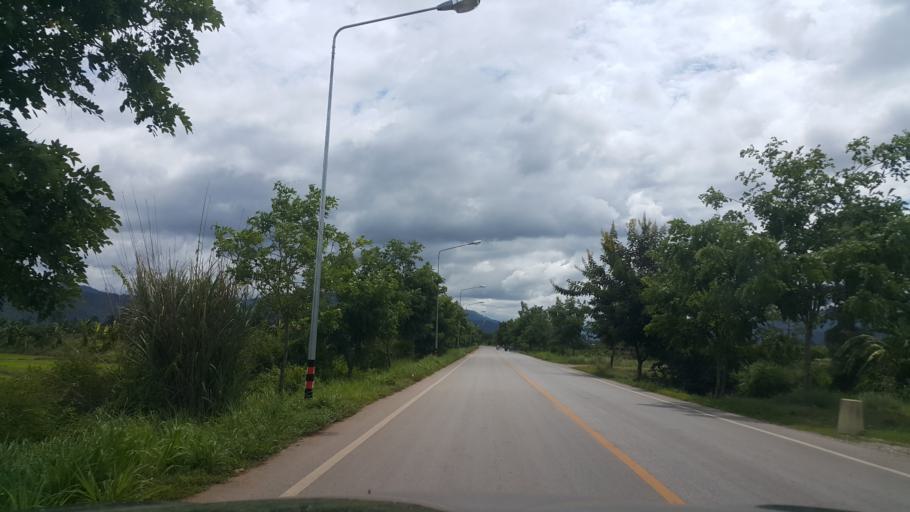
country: TH
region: Phitsanulok
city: Chat Trakan
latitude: 17.2745
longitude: 100.6134
